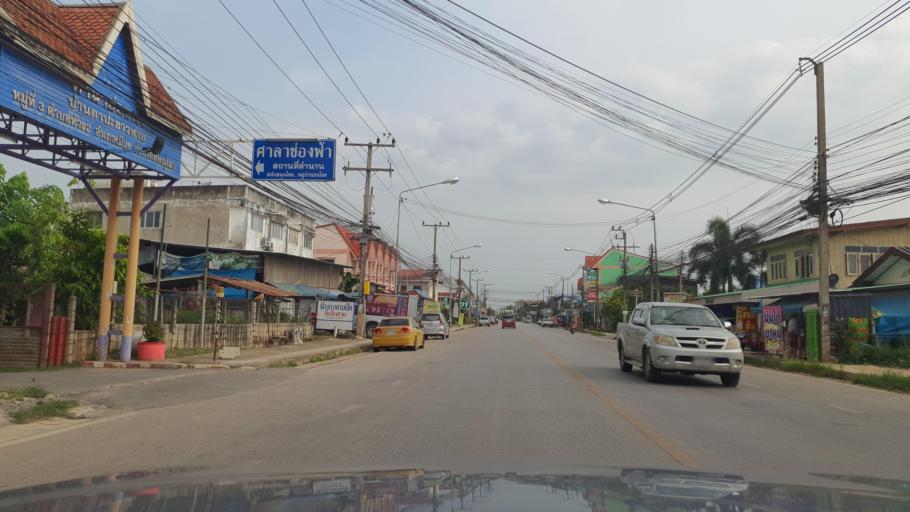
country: TH
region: Phitsanulok
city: Phitsanulok
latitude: 16.8533
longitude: 100.2542
